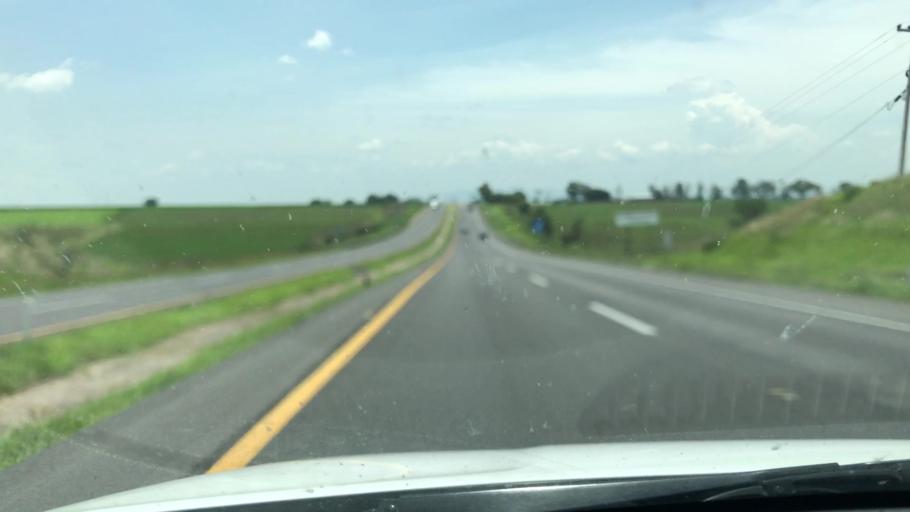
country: MX
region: Guanajuato
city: Penjamo
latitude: 20.3854
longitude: -101.7813
